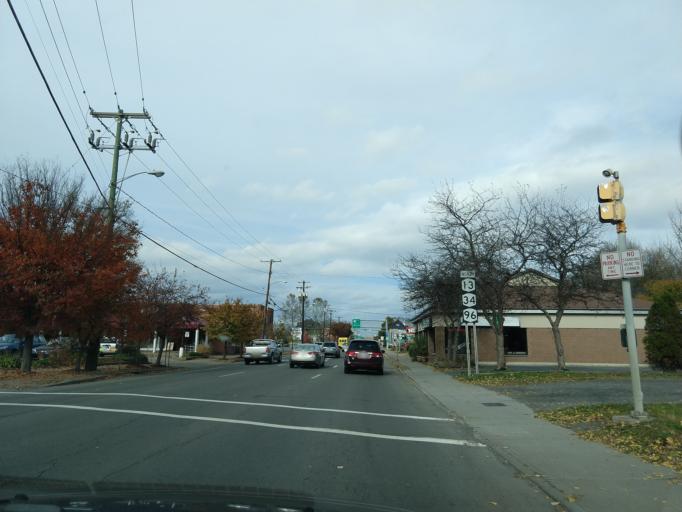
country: US
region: New York
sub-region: Tompkins County
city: Ithaca
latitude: 42.4368
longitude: -76.5082
